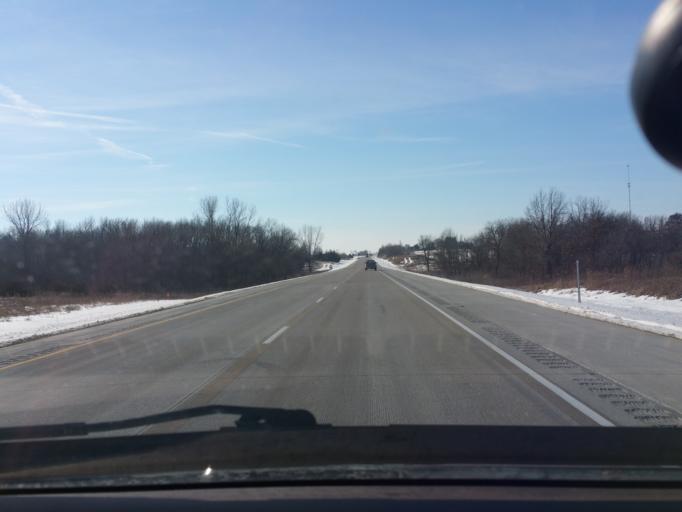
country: US
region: Iowa
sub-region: Decatur County
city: Lamoni
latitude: 40.6004
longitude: -93.9127
